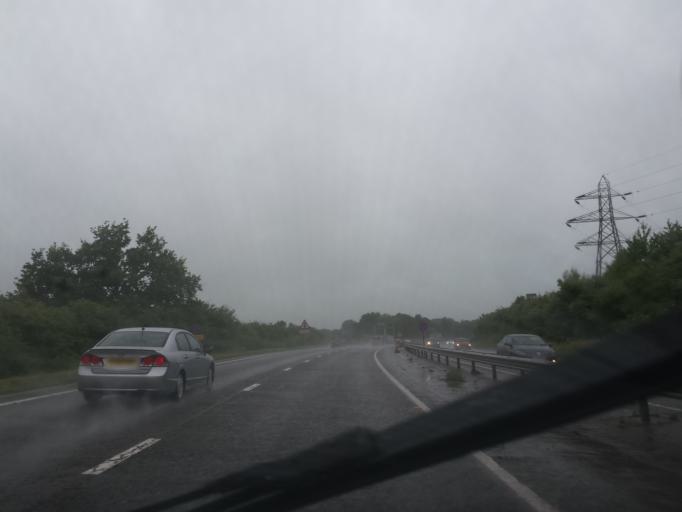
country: GB
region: England
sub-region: Warwickshire
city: Ryton on Dunsmore
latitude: 52.4005
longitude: -1.4310
